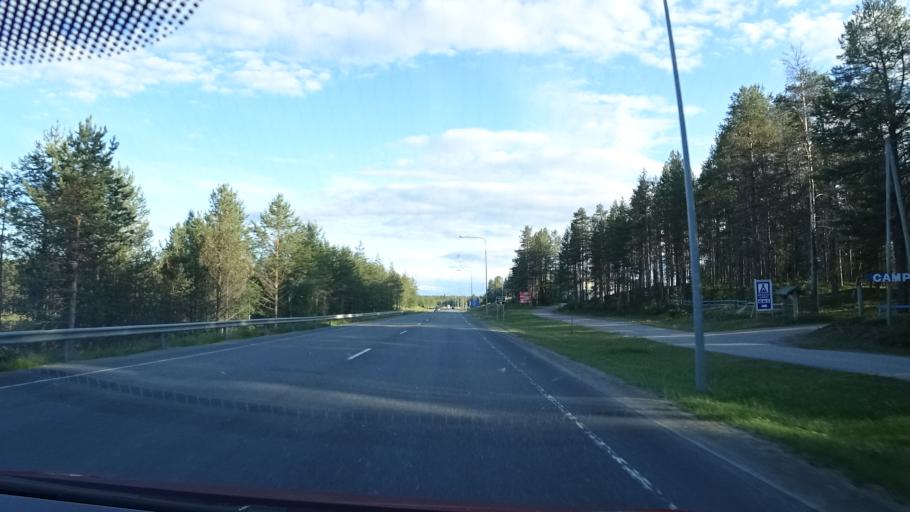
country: FI
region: Northern Ostrobothnia
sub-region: Koillismaa
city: Kuusamo
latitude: 66.0035
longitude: 29.1524
